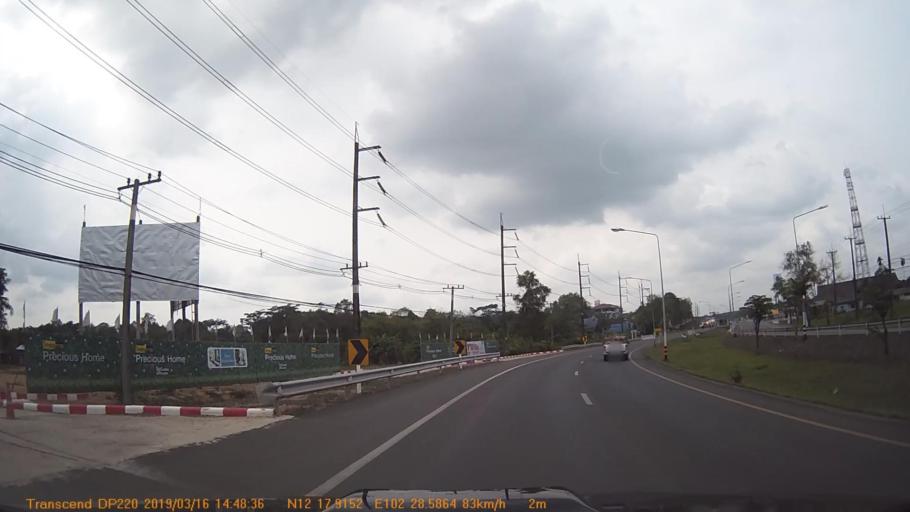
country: TH
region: Trat
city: Trat
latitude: 12.2985
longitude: 102.4764
